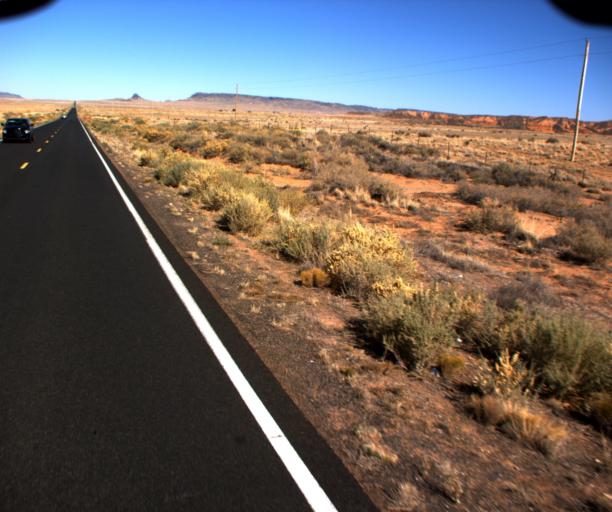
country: US
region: Arizona
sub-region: Navajo County
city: Dilkon
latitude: 35.3287
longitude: -110.4234
